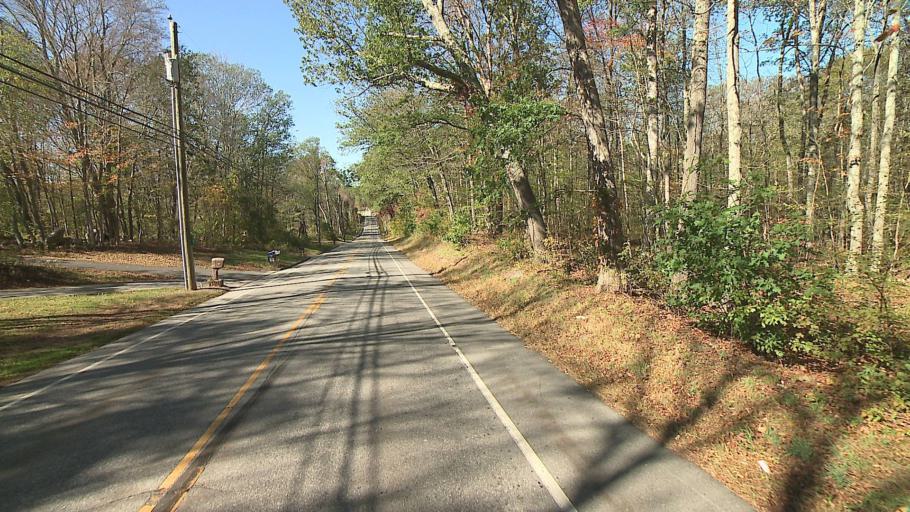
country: US
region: Connecticut
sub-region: Tolland County
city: Hebron
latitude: 41.6474
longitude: -72.4139
